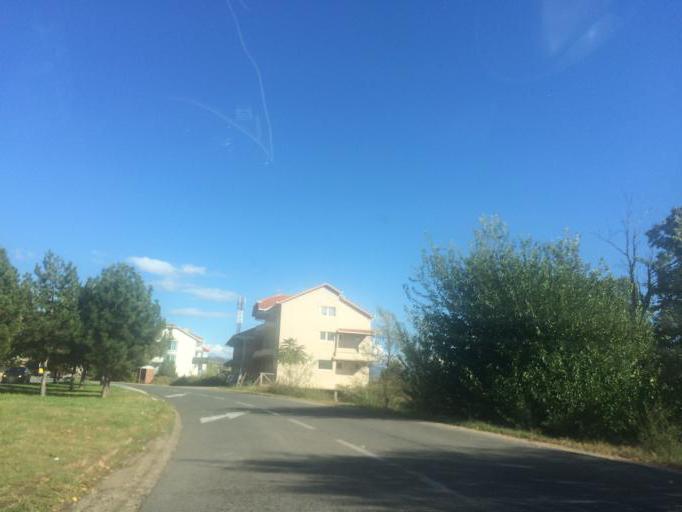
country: MK
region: Kocani
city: Orizari
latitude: 41.9133
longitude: 22.4371
